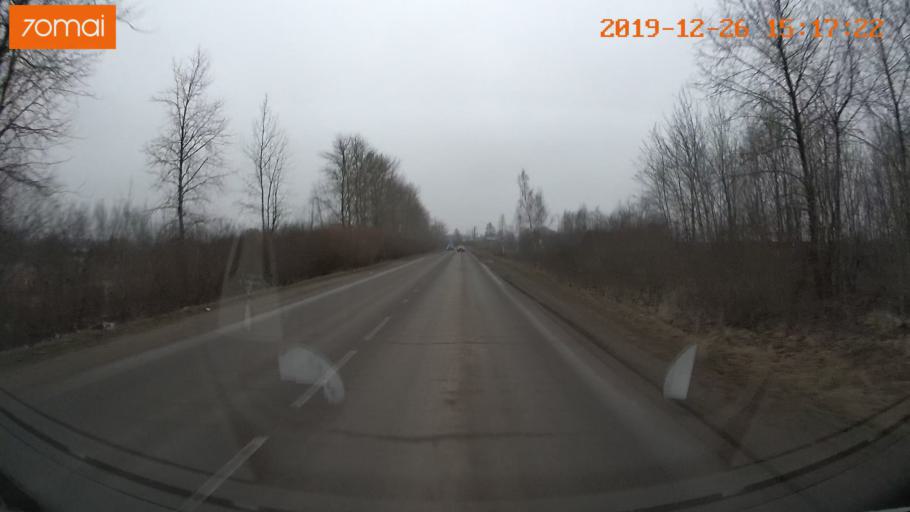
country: RU
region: Jaroslavl
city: Rybinsk
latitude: 58.0778
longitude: 38.8518
